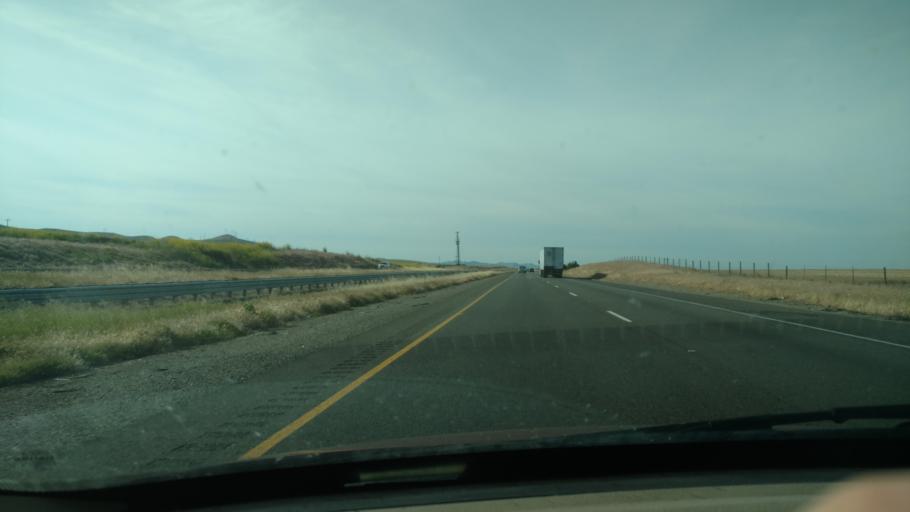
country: US
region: California
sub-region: Merced County
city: Gustine
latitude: 37.1883
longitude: -121.0702
